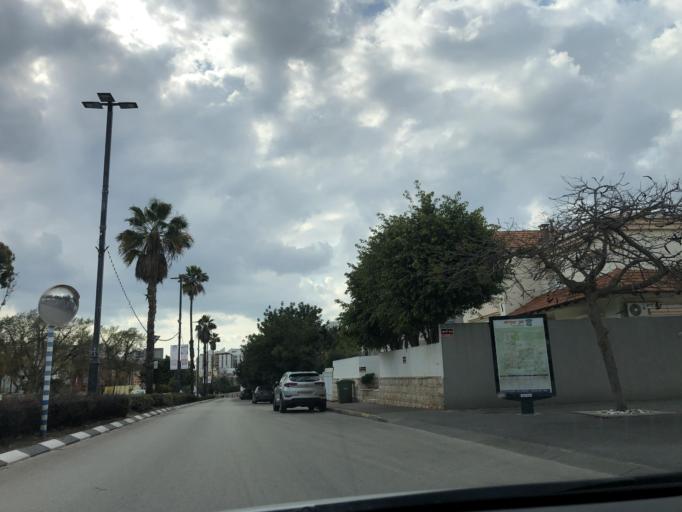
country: IL
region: Central District
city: Ganne Tiqwa
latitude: 32.0574
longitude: 34.8731
